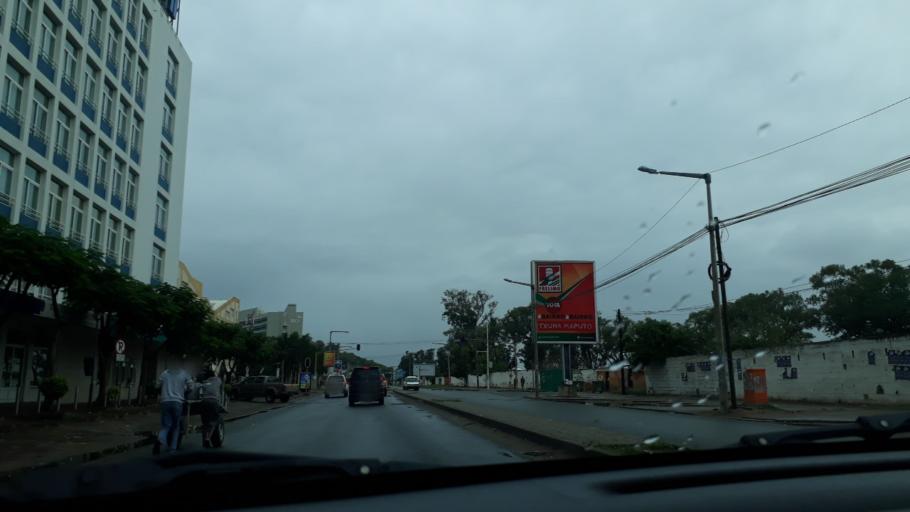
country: MZ
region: Maputo City
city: Maputo
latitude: -25.9773
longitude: 32.5794
